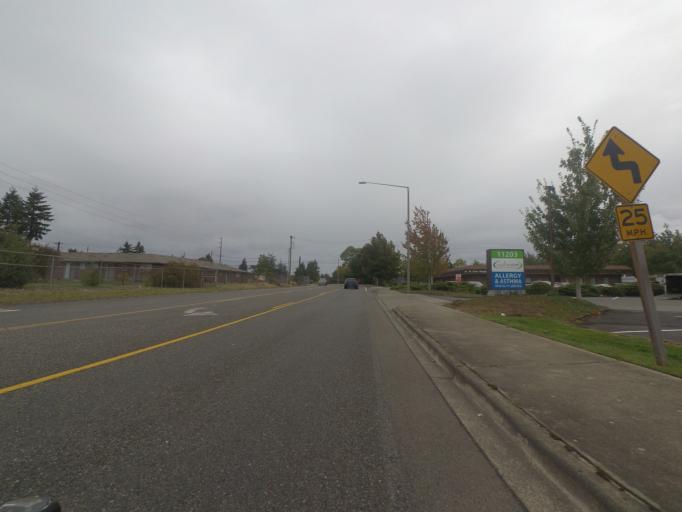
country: US
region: Washington
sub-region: Pierce County
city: Lakewood
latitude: 47.1558
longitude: -122.5033
